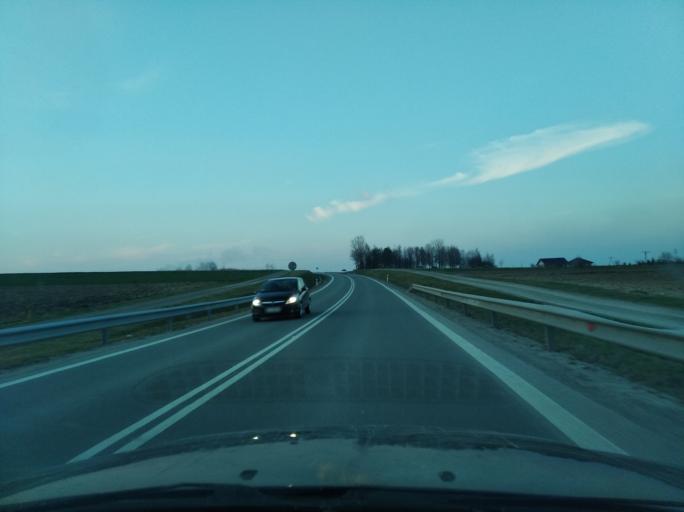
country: PL
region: Subcarpathian Voivodeship
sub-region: Powiat przeworski
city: Grzeska
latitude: 50.0653
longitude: 22.4703
